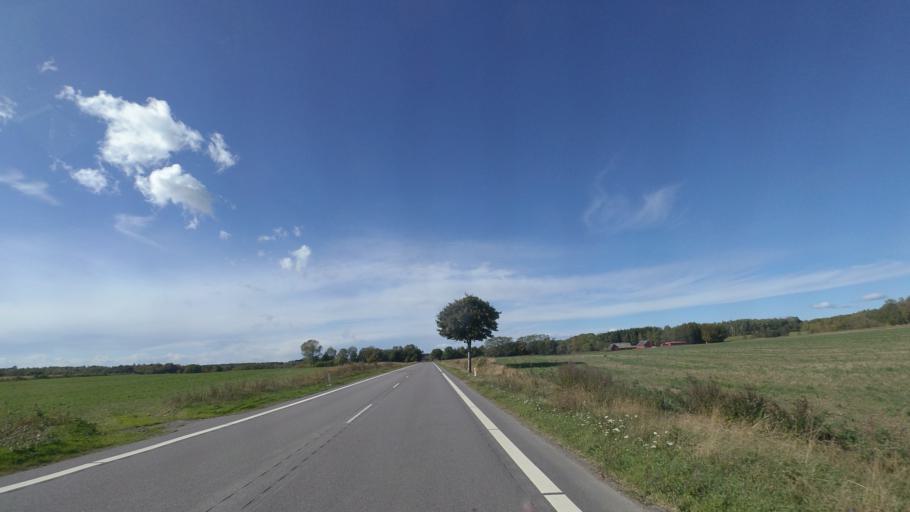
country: DK
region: Capital Region
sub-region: Bornholm Kommune
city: Ronne
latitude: 55.0754
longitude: 14.7778
